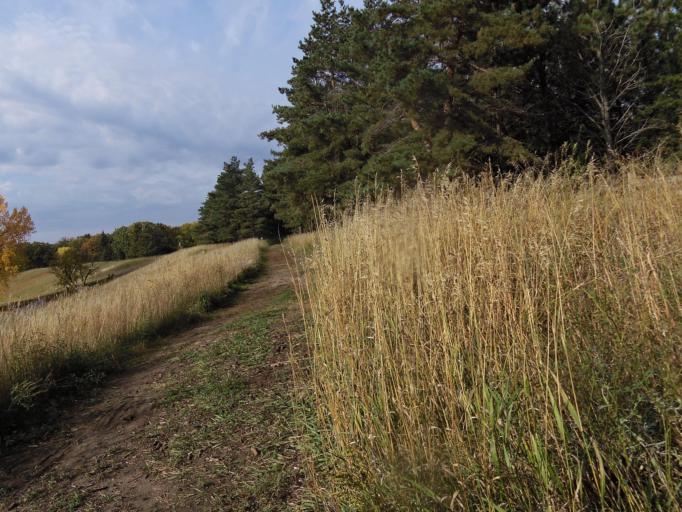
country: US
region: North Dakota
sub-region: Pembina County
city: Cavalier
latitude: 48.7810
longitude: -97.7474
